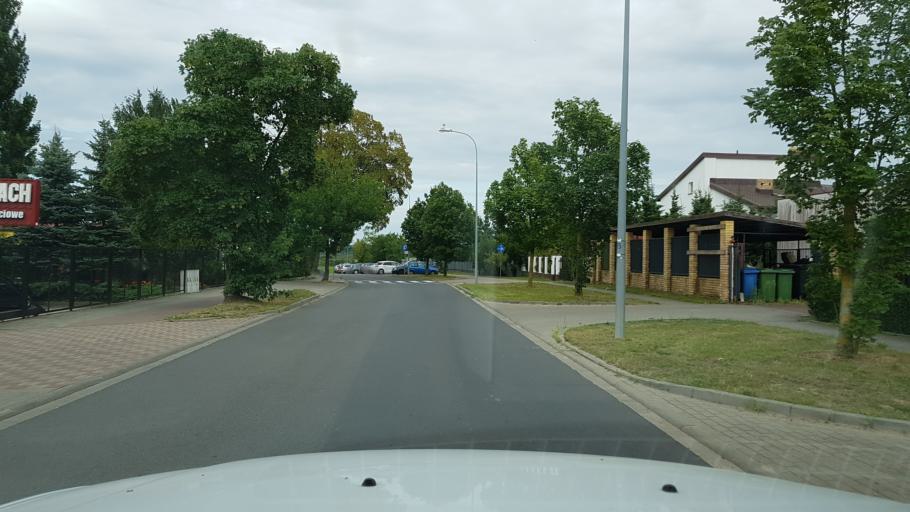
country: PL
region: West Pomeranian Voivodeship
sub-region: Powiat kolobrzeski
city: Kolobrzeg
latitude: 54.1666
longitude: 15.6018
